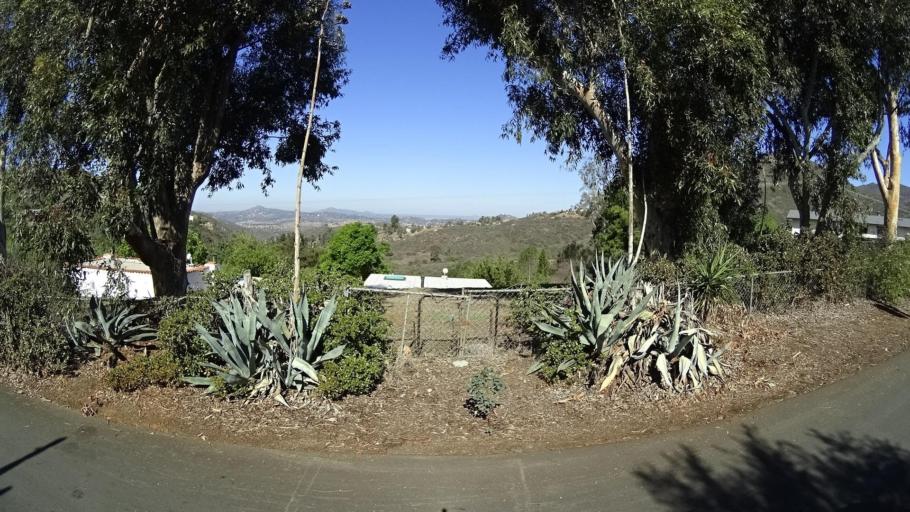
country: US
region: California
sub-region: San Diego County
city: Jamul
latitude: 32.7274
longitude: -116.8685
